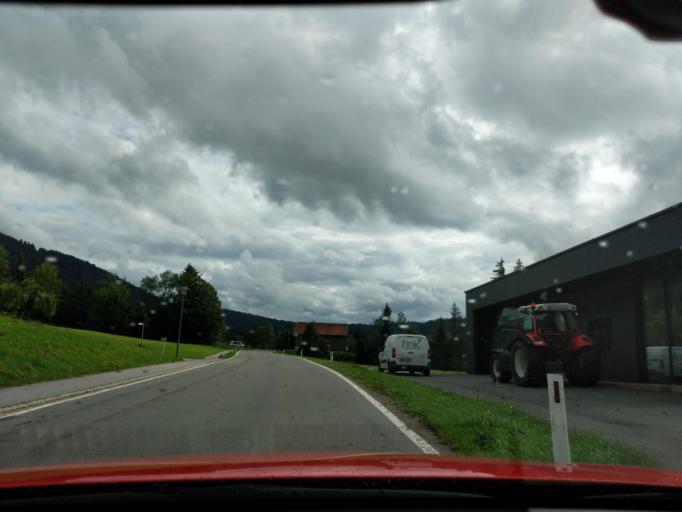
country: AT
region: Vorarlberg
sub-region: Politischer Bezirk Bregenz
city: Krumbach
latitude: 47.4972
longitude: 9.9464
